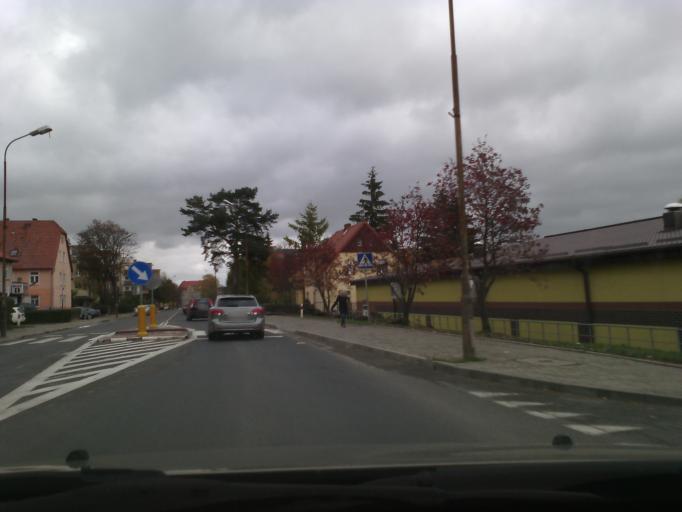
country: PL
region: Lower Silesian Voivodeship
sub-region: Powiat kamiennogorski
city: Kamienna Gora
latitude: 50.7799
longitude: 16.0177
